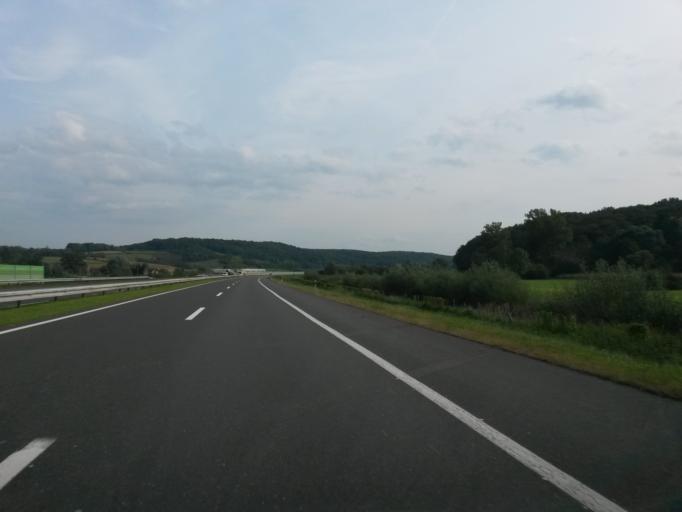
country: HR
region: Varazdinska
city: Remetinec
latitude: 46.0784
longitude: 16.2911
